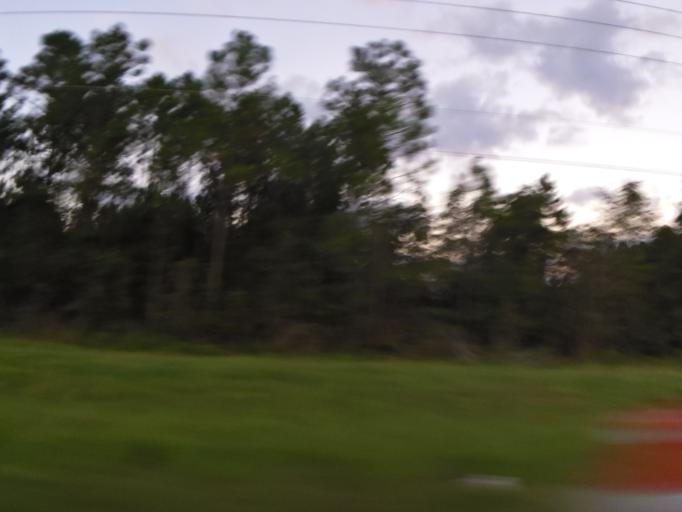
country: US
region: Florida
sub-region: Saint Johns County
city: Palm Valley
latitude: 30.0842
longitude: -81.4650
